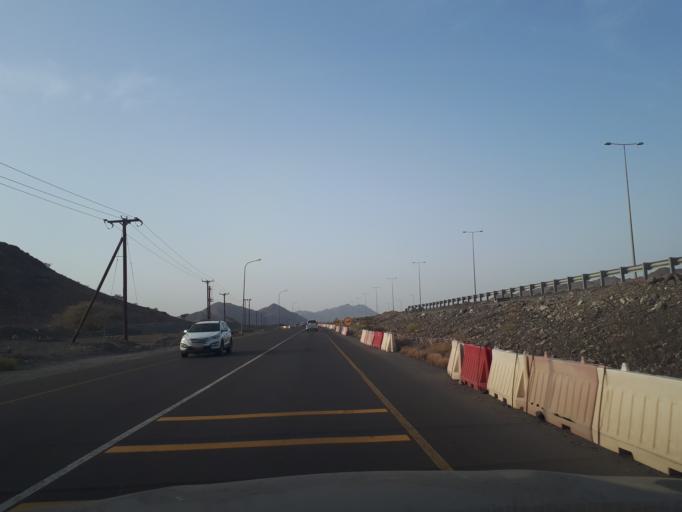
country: OM
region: Muhafazat ad Dakhiliyah
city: Sufalat Sama'il
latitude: 23.2859
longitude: 58.1084
